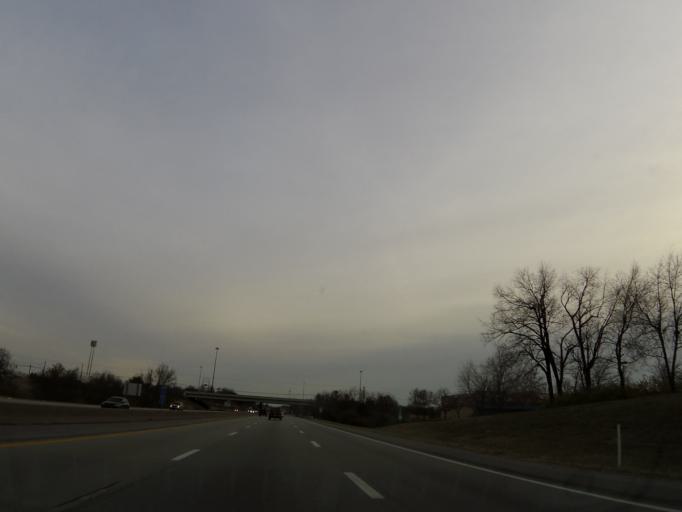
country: US
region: Kentucky
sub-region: Scott County
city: Georgetown
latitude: 38.2184
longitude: -84.5356
